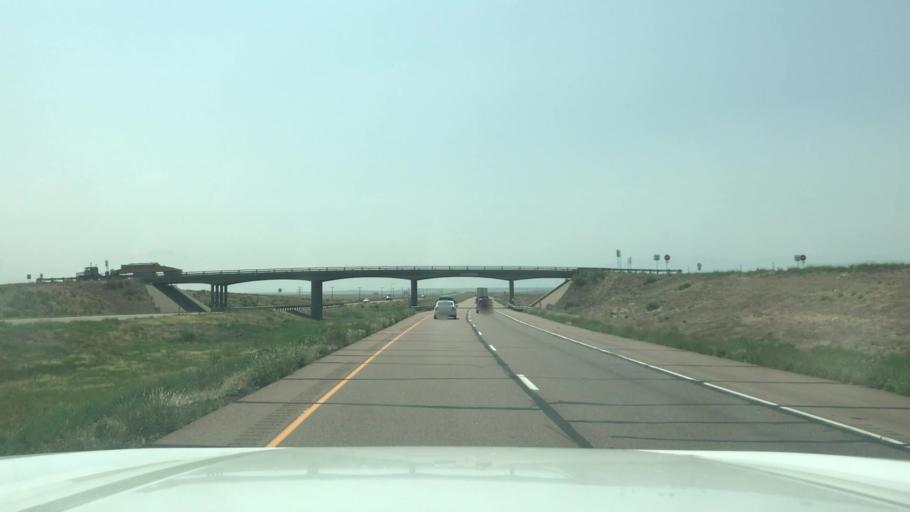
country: US
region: Colorado
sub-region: Pueblo County
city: Pueblo
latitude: 38.1620
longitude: -104.6431
